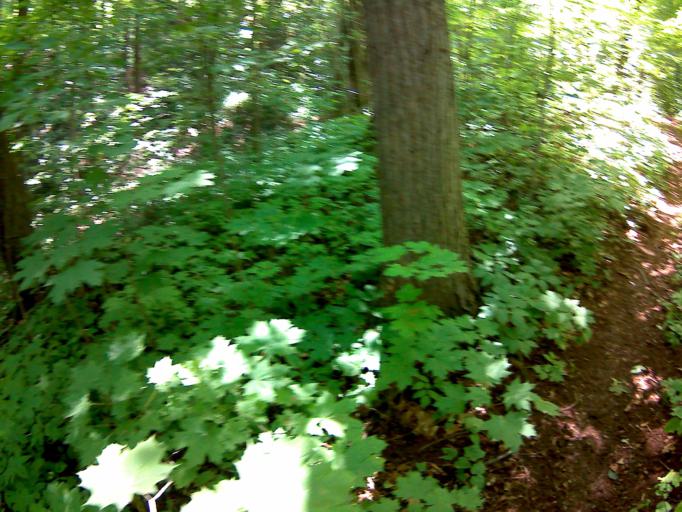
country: RU
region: Nizjnij Novgorod
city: Nizhniy Novgorod
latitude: 56.2272
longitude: 43.9223
